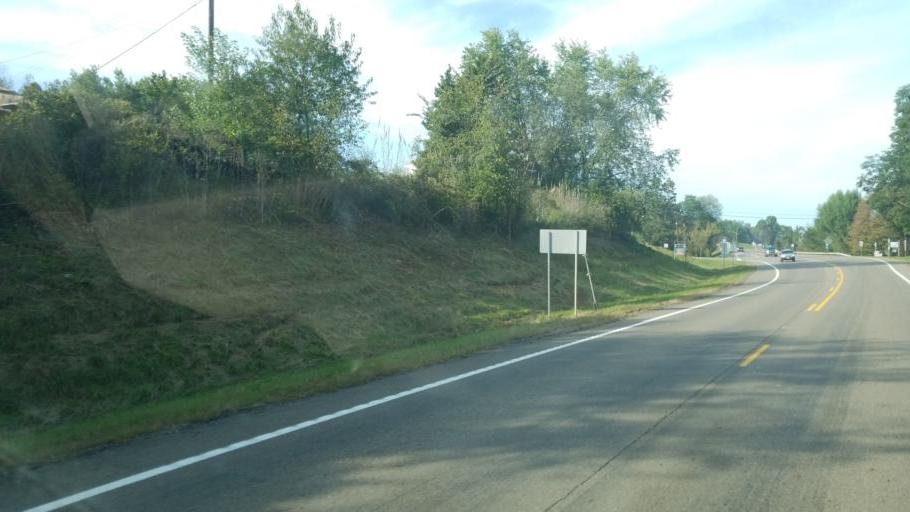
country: US
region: Ohio
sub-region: Knox County
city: Oak Hill
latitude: 40.3992
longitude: -82.2764
